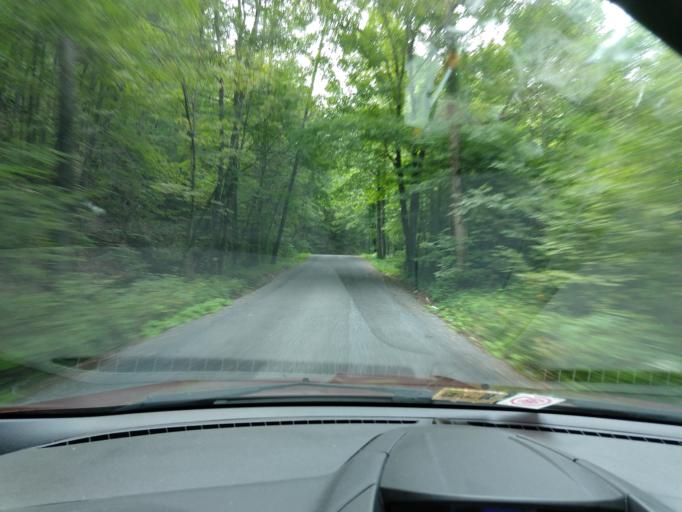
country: US
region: Virginia
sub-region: City of Covington
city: Covington
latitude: 37.9214
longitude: -80.0744
